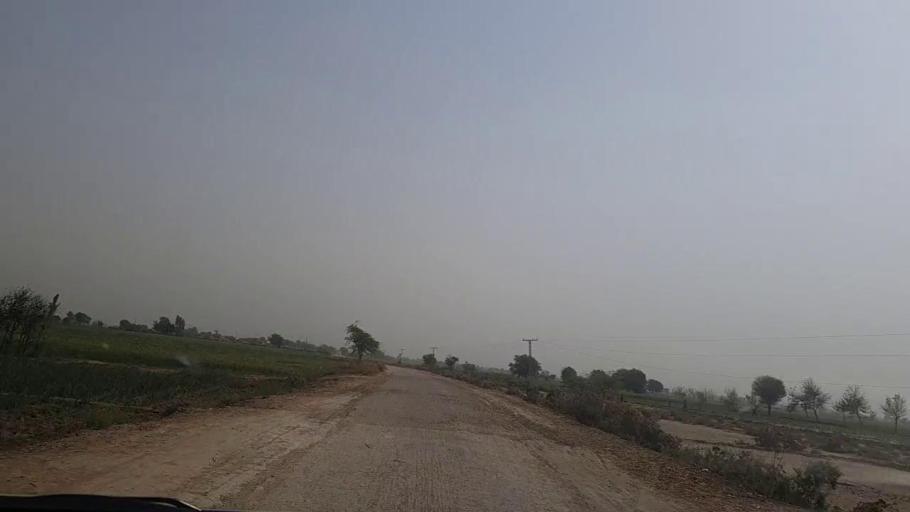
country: PK
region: Sindh
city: Pithoro
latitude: 25.4861
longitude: 69.2167
